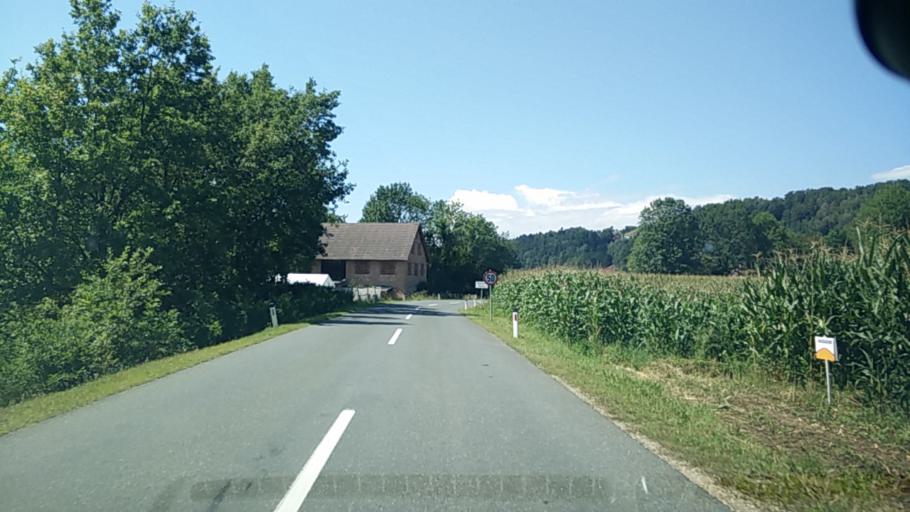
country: AT
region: Carinthia
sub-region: Politischer Bezirk Volkermarkt
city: Sittersdorf
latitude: 46.5561
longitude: 14.5705
